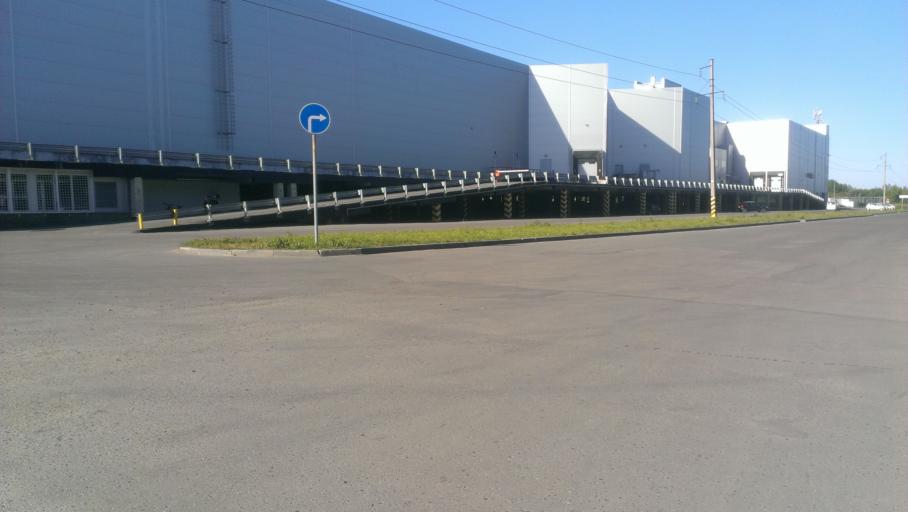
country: RU
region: Altai Krai
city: Novosilikatnyy
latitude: 53.3250
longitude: 83.6895
